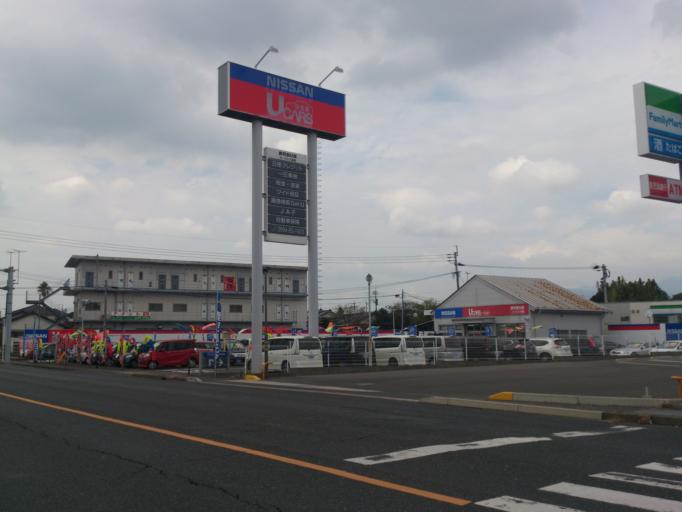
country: JP
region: Kagoshima
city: Kanoya
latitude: 31.3888
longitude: 130.8960
